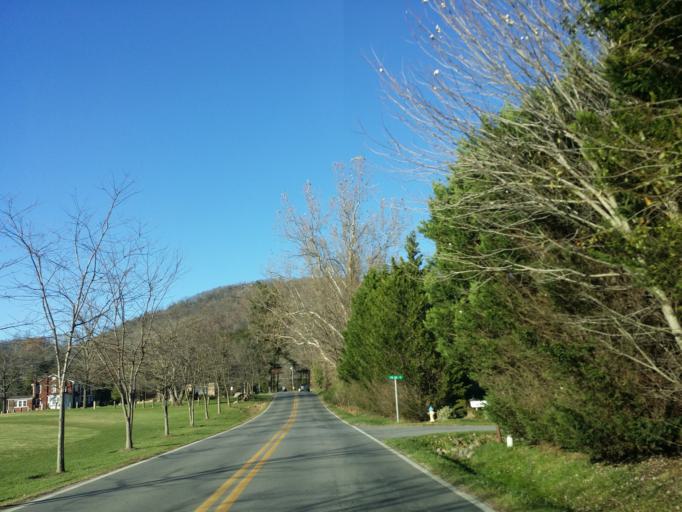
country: US
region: North Carolina
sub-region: Buncombe County
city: Swannanoa
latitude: 35.6030
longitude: -82.4079
